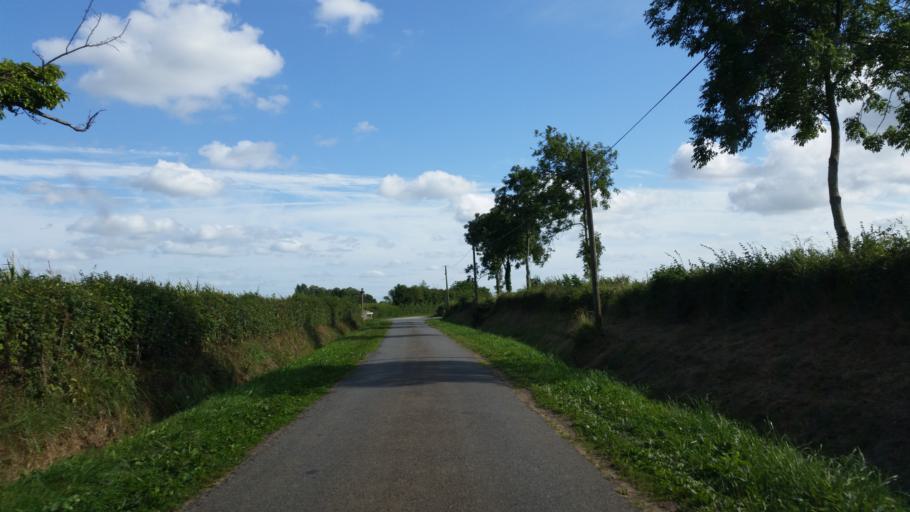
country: FR
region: Lower Normandy
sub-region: Departement de la Manche
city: Sainte-Mere-Eglise
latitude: 49.4530
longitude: -1.2917
